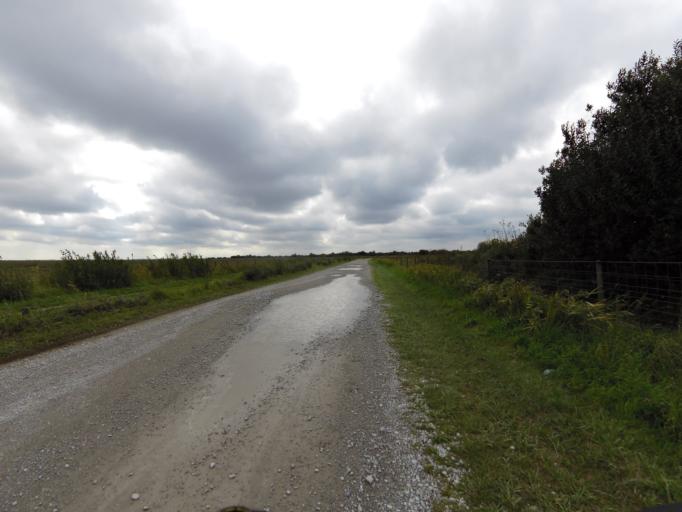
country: NL
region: South Holland
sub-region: Gemeente Goeree-Overflakkee
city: Dirksland
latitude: 51.7583
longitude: 4.0337
